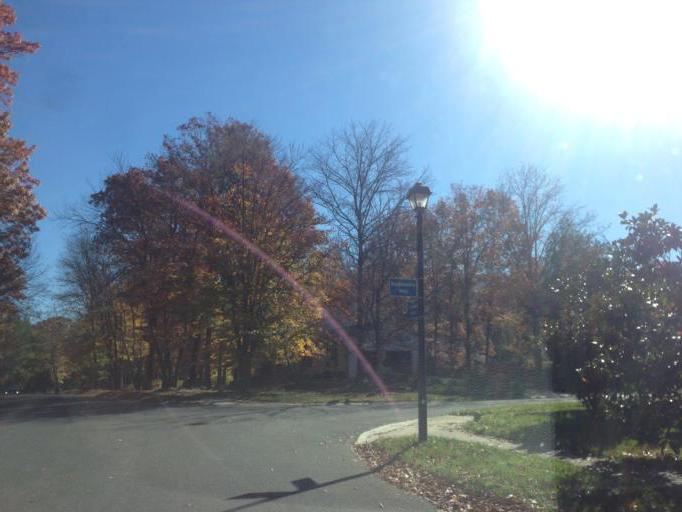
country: US
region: Maryland
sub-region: Howard County
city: Riverside
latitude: 39.1975
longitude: -76.8762
